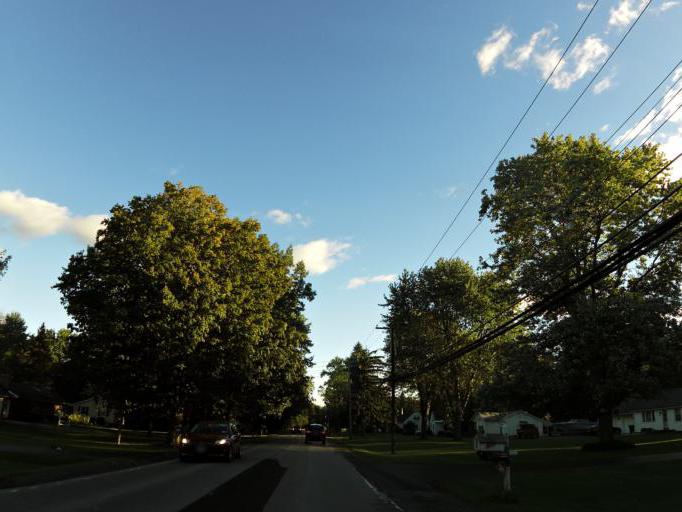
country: US
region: New York
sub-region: Erie County
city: Billington Heights
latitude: 42.7899
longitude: -78.6209
